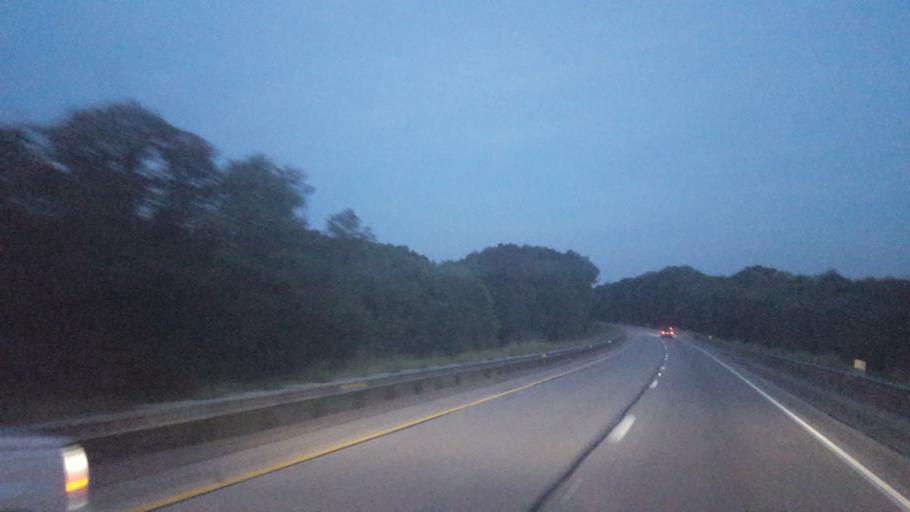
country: US
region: Pennsylvania
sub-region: Mercer County
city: Grove City
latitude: 41.2048
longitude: -79.9248
